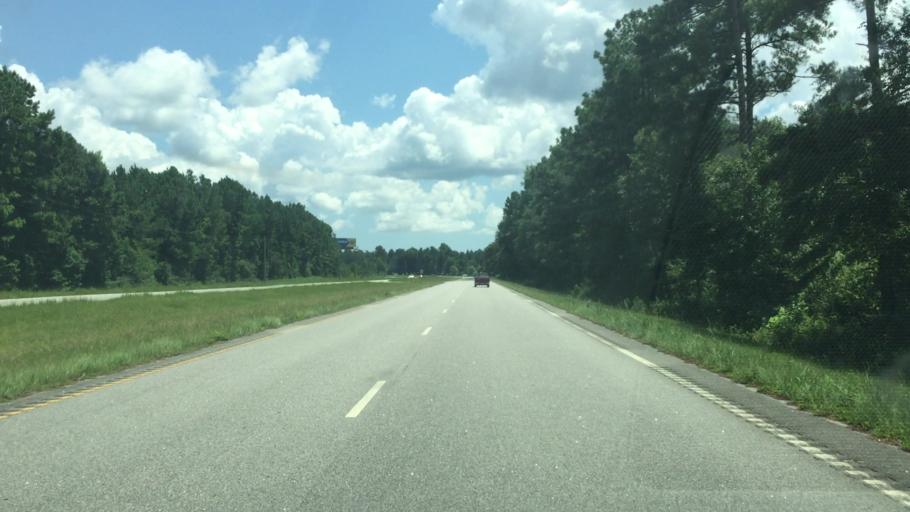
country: US
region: South Carolina
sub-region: Horry County
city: Loris
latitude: 34.0225
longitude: -78.7972
